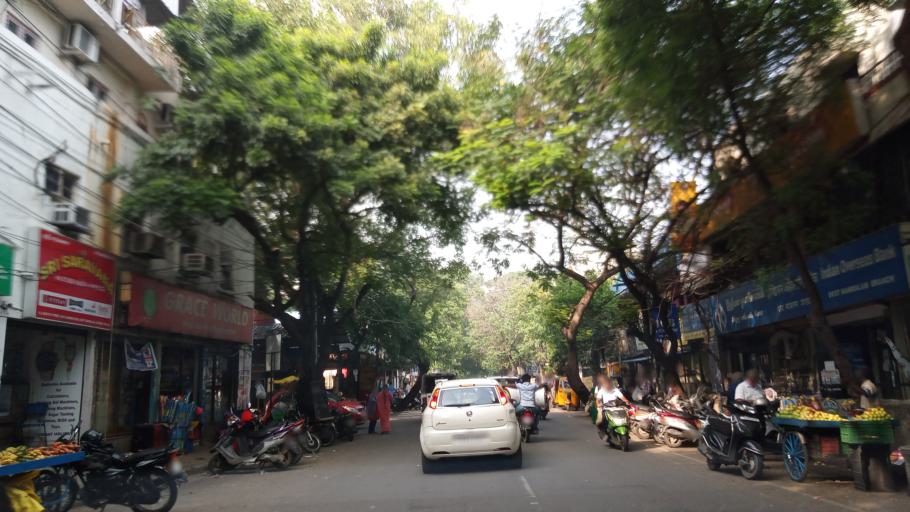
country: IN
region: Tamil Nadu
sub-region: Chennai
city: Chetput
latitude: 13.0386
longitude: 80.2211
